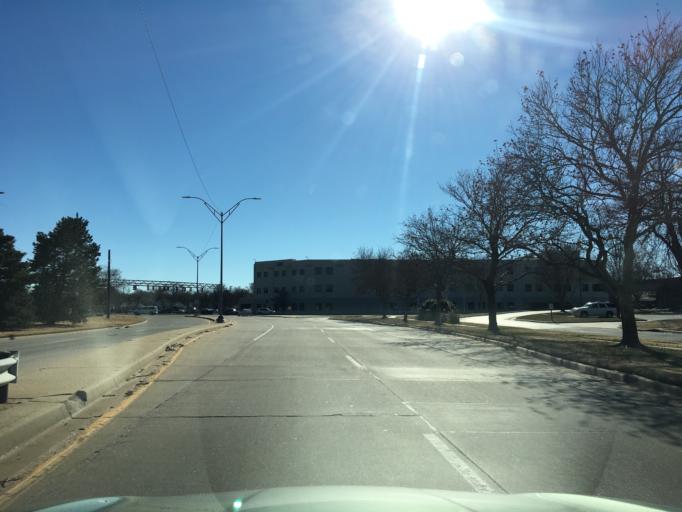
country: US
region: Kansas
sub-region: Sedgwick County
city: Wichita
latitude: 37.6732
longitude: -97.3083
